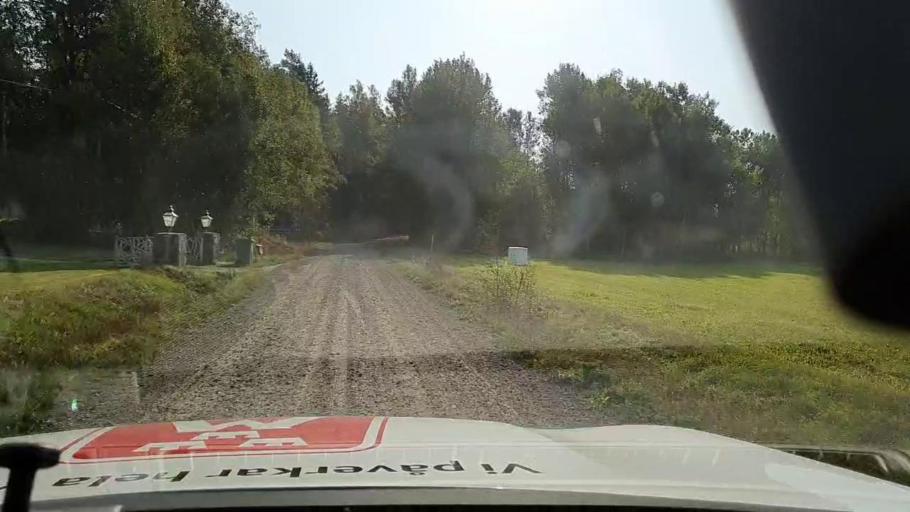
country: SE
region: Vaestmanland
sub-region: Kungsors Kommun
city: Kungsoer
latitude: 59.3488
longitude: 16.1668
